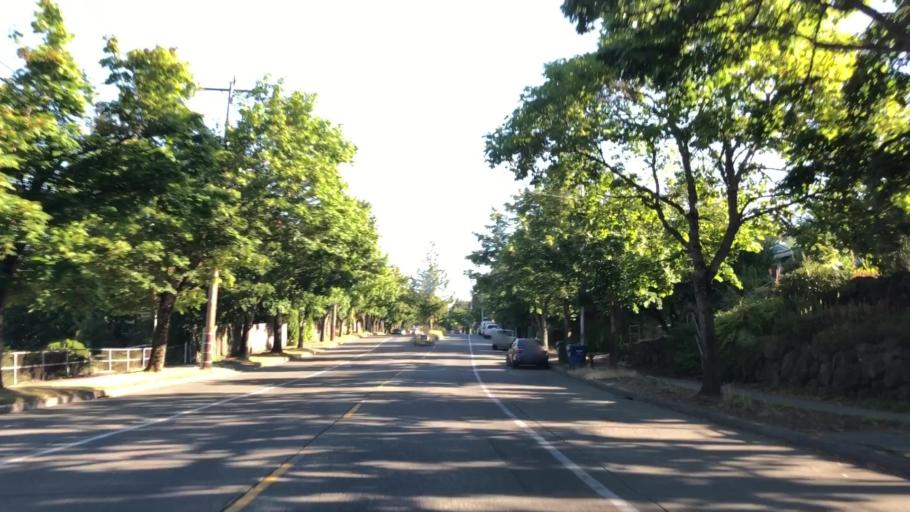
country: US
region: Washington
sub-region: King County
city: White Center
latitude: 47.5434
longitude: -122.3550
